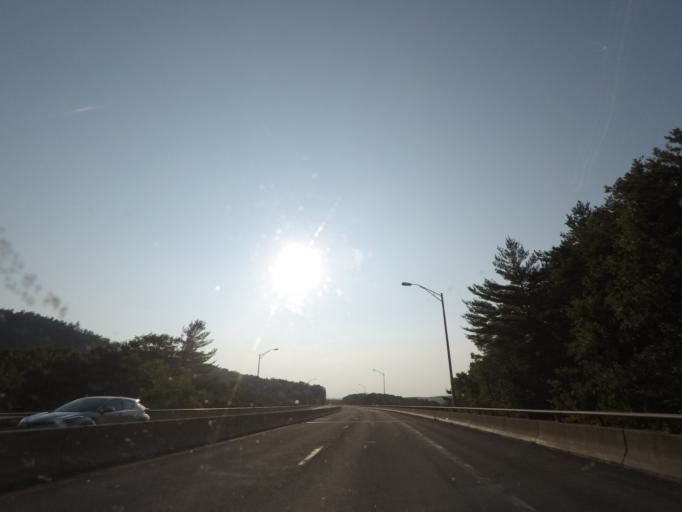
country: US
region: Massachusetts
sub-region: Hampden County
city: Westfield
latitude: 42.1569
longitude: -72.8174
